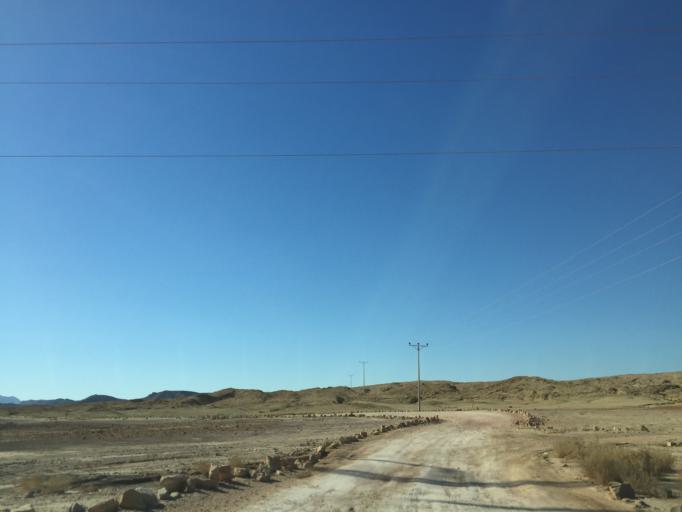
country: IL
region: Southern District
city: Mitzpe Ramon
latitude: 30.6183
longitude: 34.9171
